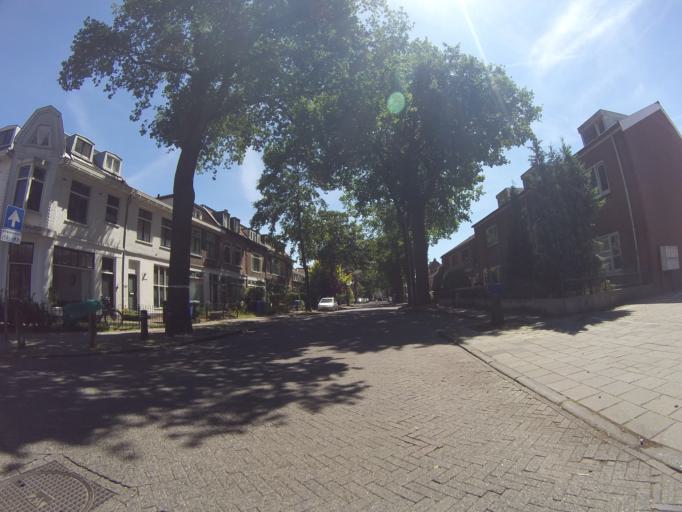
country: NL
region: Utrecht
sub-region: Gemeente Amersfoort
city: Amersfoort
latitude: 52.1568
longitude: 5.3706
